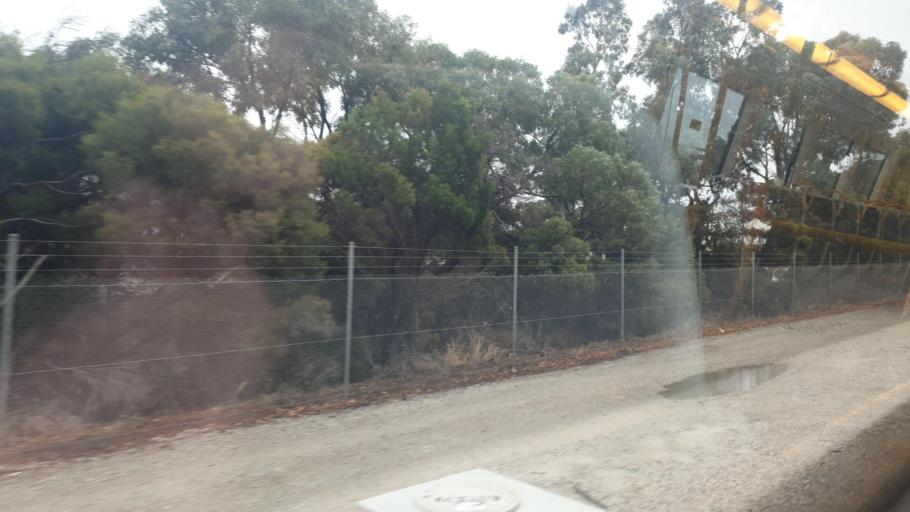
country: AU
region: Western Australia
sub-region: Fremantle
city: North Fremantle
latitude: -32.0356
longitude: 115.7518
